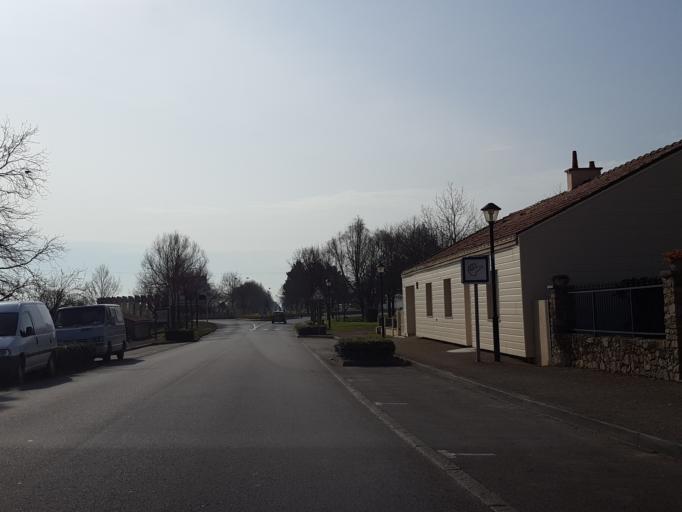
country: FR
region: Pays de la Loire
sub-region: Departement de la Vendee
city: Les Lucs-sur-Boulogne
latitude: 46.8406
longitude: -1.4916
